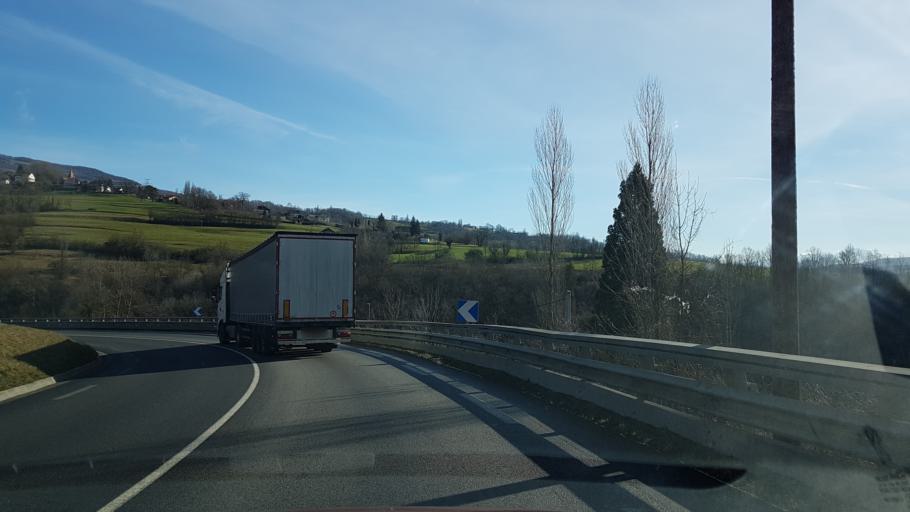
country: FR
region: Rhone-Alpes
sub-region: Departement de la Haute-Savoie
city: Frangy
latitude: 46.0313
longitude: 5.8887
